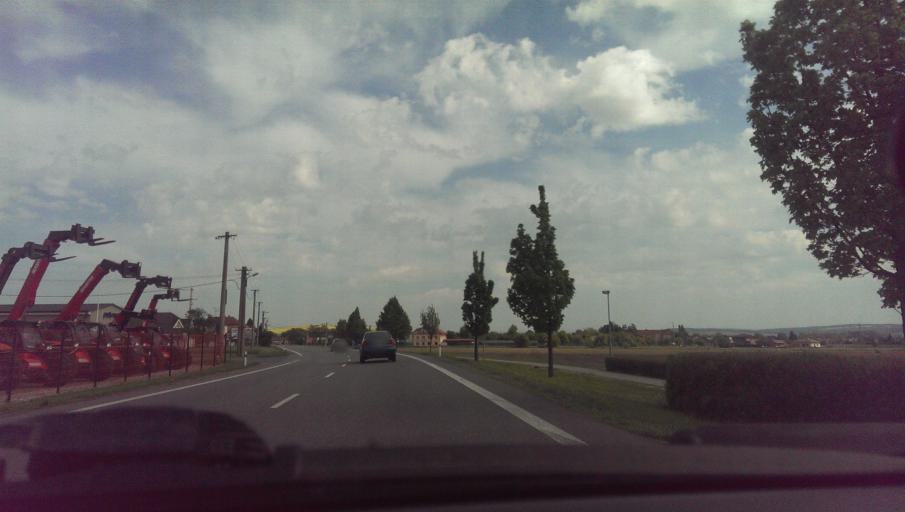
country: CZ
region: Zlin
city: Babice
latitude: 49.1135
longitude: 17.4692
